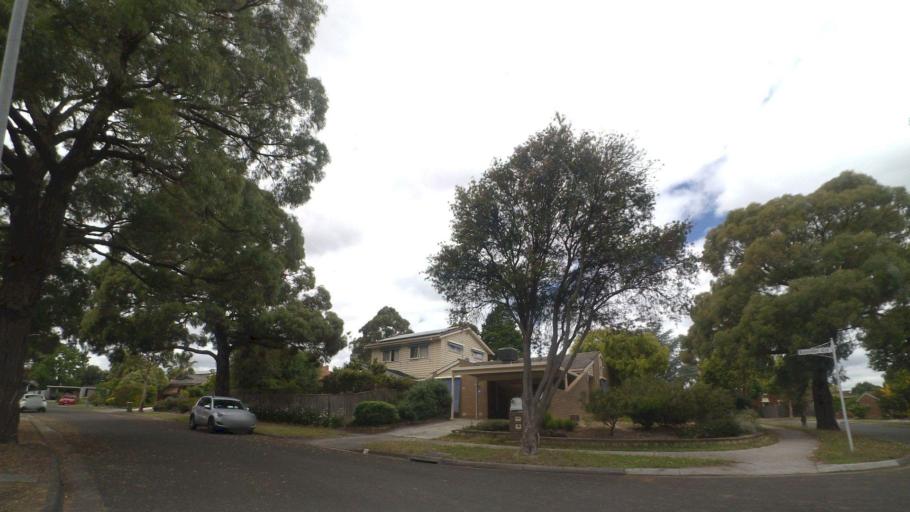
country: AU
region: Victoria
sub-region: Knox
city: Wantirna
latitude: -37.8641
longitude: 145.2399
